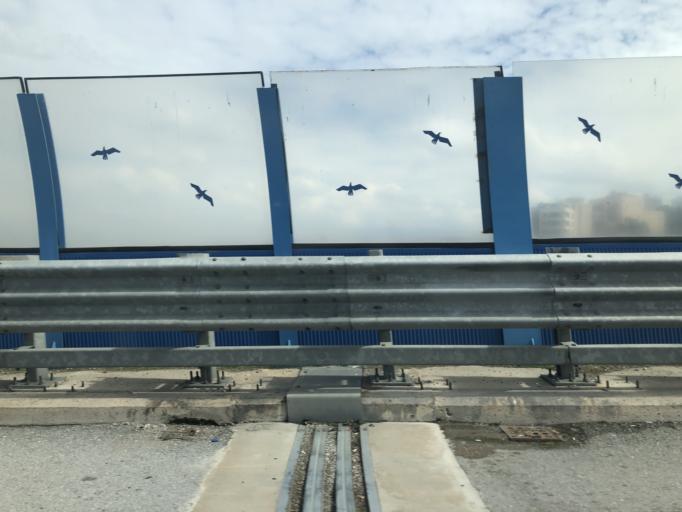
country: TR
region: Izmir
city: Karabaglar
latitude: 38.3934
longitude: 27.0632
